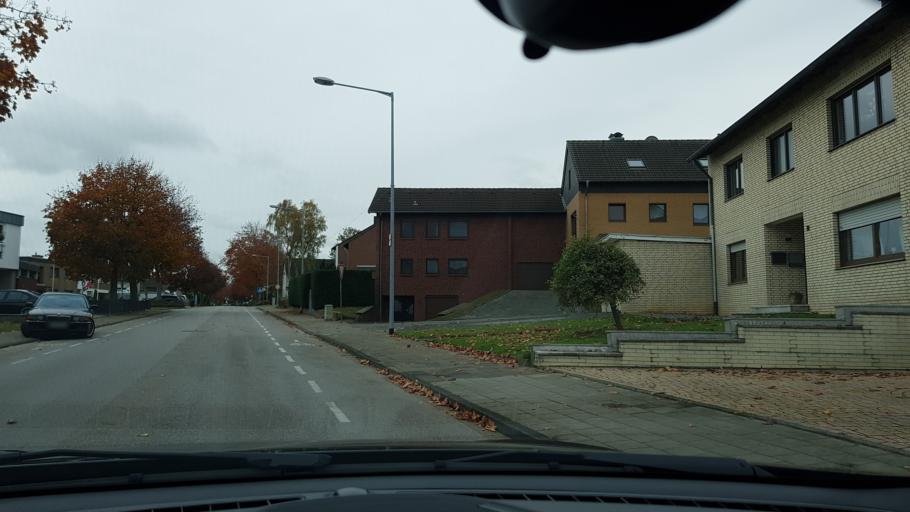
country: DE
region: North Rhine-Westphalia
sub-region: Regierungsbezirk Koln
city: Bedburg
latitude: 51.0038
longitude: 6.5510
